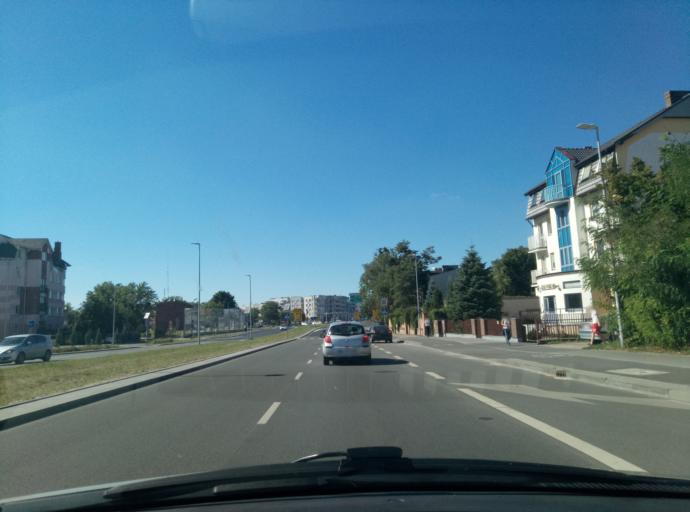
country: PL
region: Kujawsko-Pomorskie
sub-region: Torun
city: Torun
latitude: 53.0232
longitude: 18.5940
